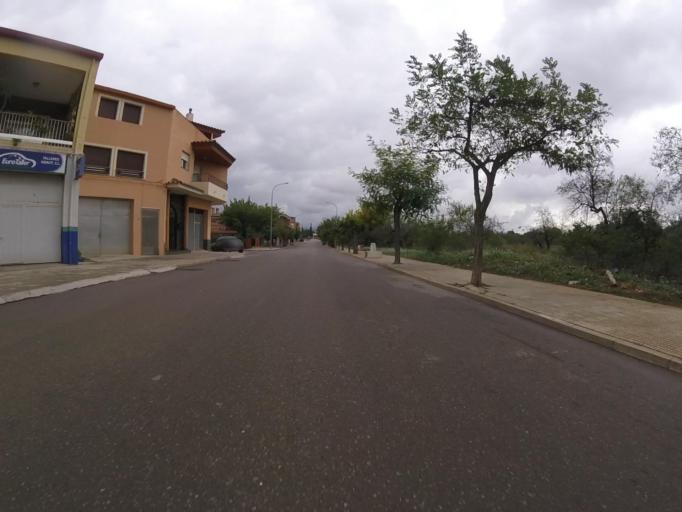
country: ES
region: Valencia
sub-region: Provincia de Castello
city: Cabanes
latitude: 40.1581
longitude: 0.0430
